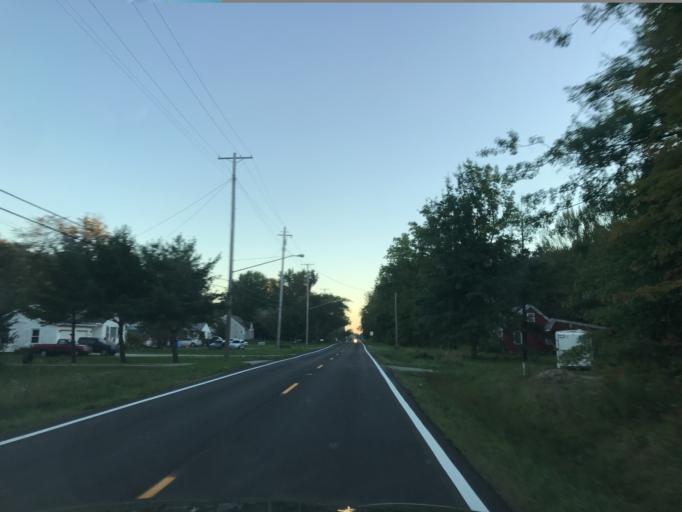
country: US
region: Ohio
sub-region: Ashtabula County
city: Ashtabula
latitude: 41.8773
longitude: -80.8574
